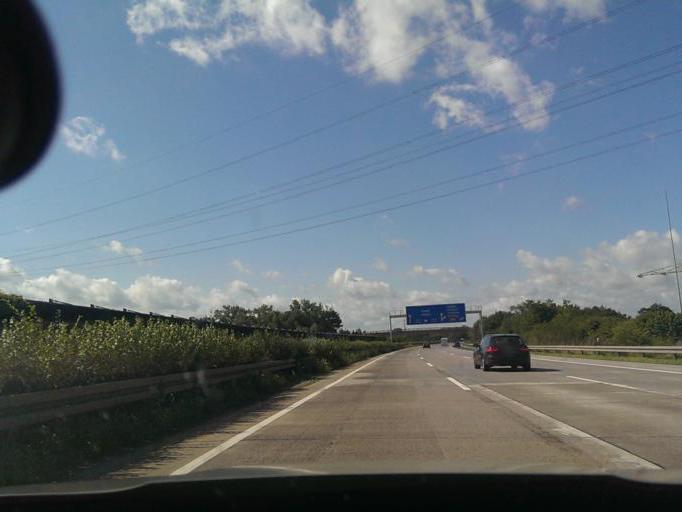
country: DE
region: Lower Saxony
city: Lehrte
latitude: 52.3663
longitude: 9.8924
